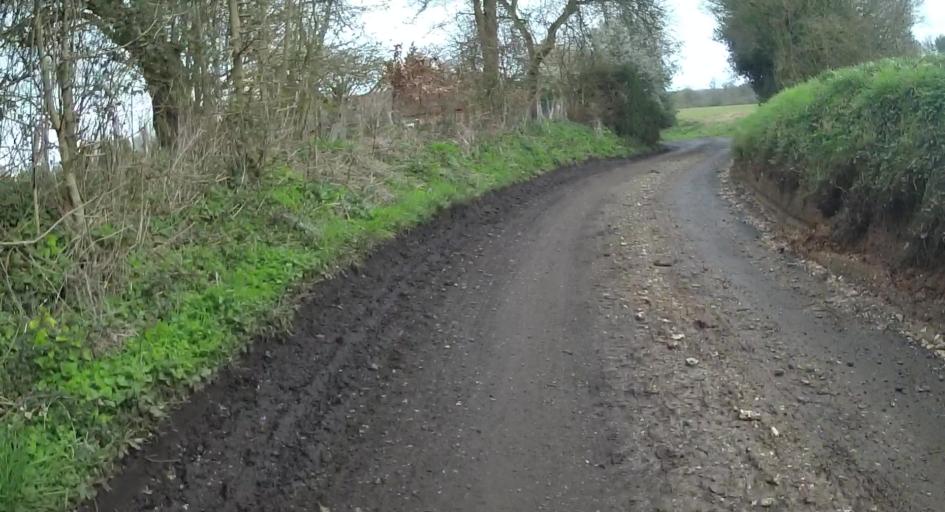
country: GB
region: England
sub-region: Hampshire
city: Kingsclere
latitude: 51.3198
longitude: -1.2184
